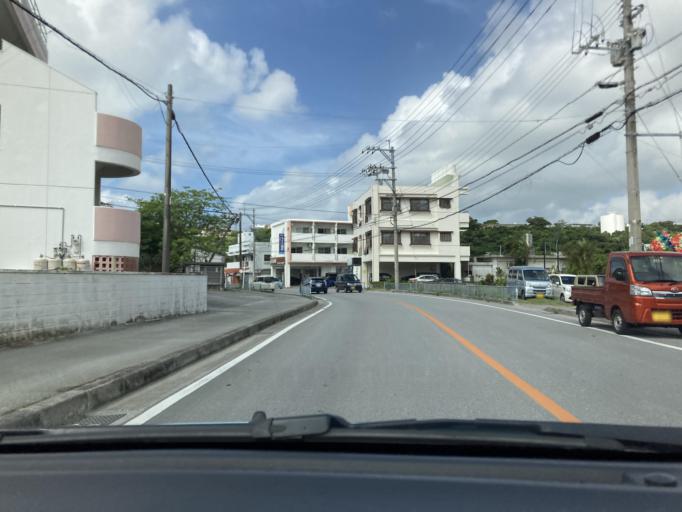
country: JP
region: Okinawa
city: Okinawa
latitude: 26.3200
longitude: 127.8071
